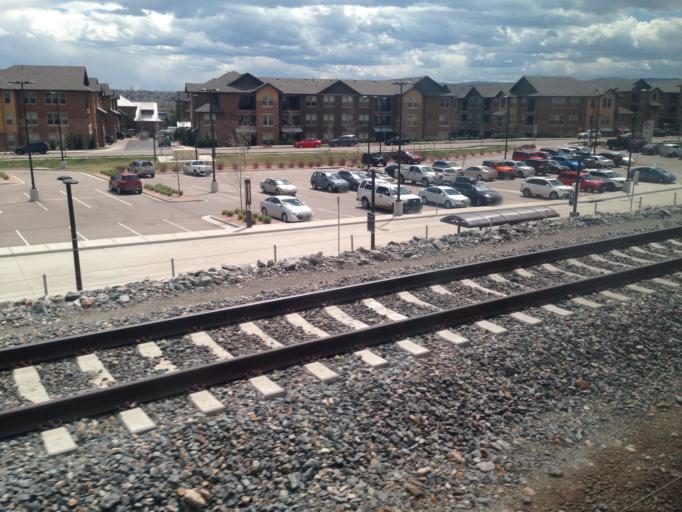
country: US
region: Colorado
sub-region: Jefferson County
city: Arvada
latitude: 39.7925
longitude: -105.1111
